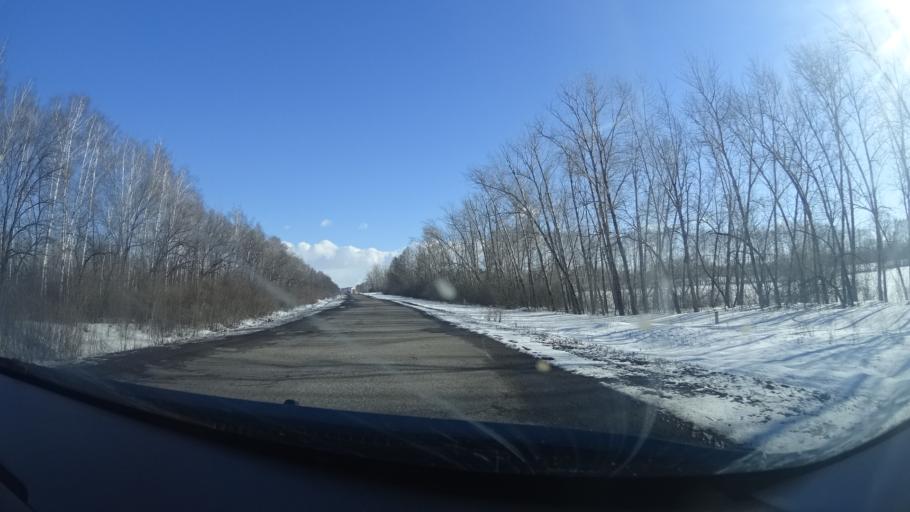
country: RU
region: Bashkortostan
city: Chishmy
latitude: 54.5979
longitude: 55.3531
